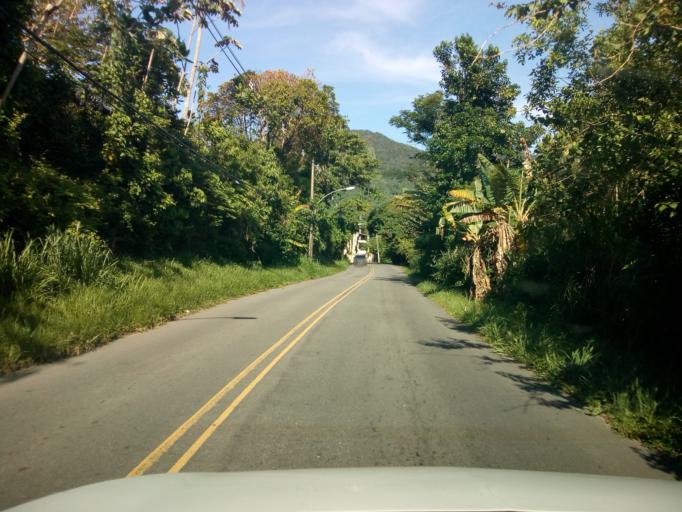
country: BR
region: Rio de Janeiro
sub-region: Nilopolis
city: Nilopolis
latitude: -23.0256
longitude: -43.5116
